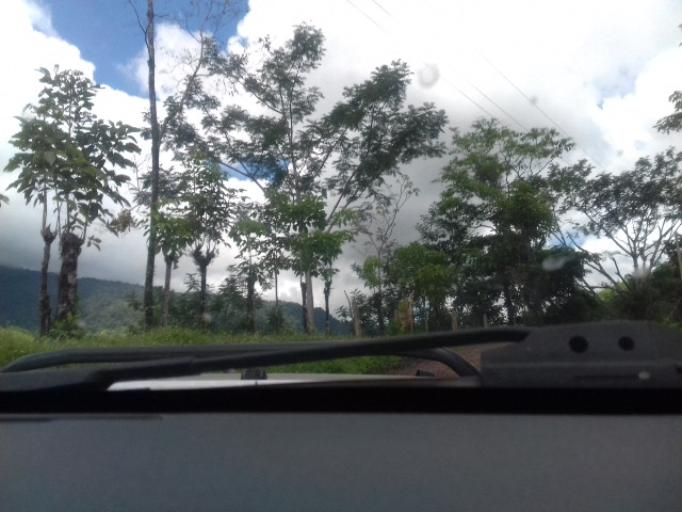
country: NI
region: Matagalpa
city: Rio Blanco
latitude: 13.0045
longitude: -85.2028
